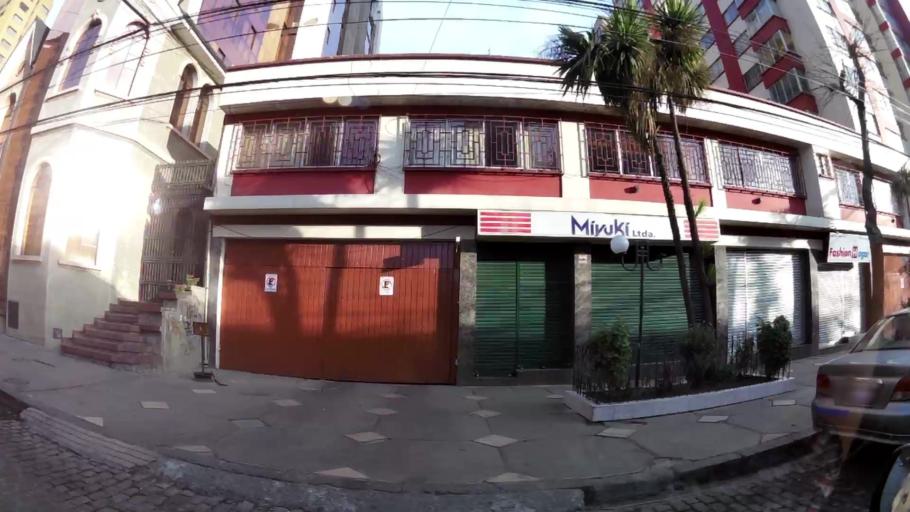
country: BO
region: La Paz
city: La Paz
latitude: -16.5078
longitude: -68.1281
